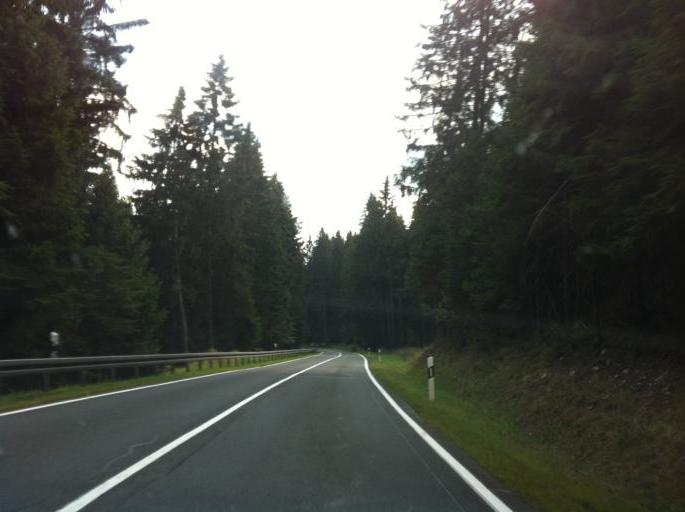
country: DE
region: Thuringia
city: Steinheid
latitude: 50.4849
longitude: 11.0974
